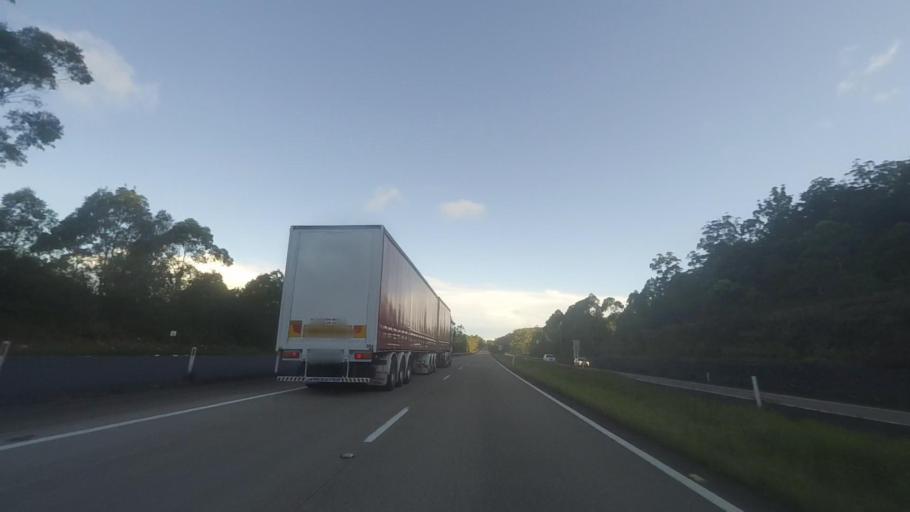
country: AU
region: New South Wales
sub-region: Great Lakes
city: Bulahdelah
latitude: -32.2879
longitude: 152.3413
